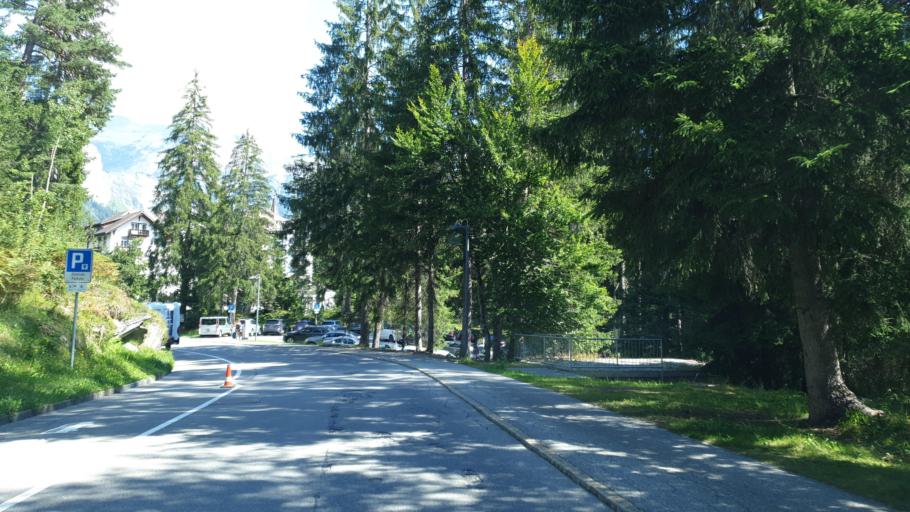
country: CH
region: Grisons
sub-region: Imboden District
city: Flims
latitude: 46.8252
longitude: 9.2899
